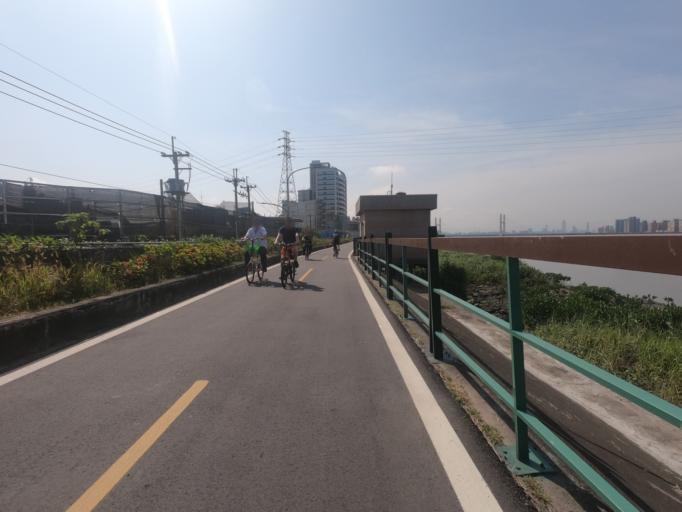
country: TW
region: Taipei
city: Taipei
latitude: 25.0938
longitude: 121.4965
